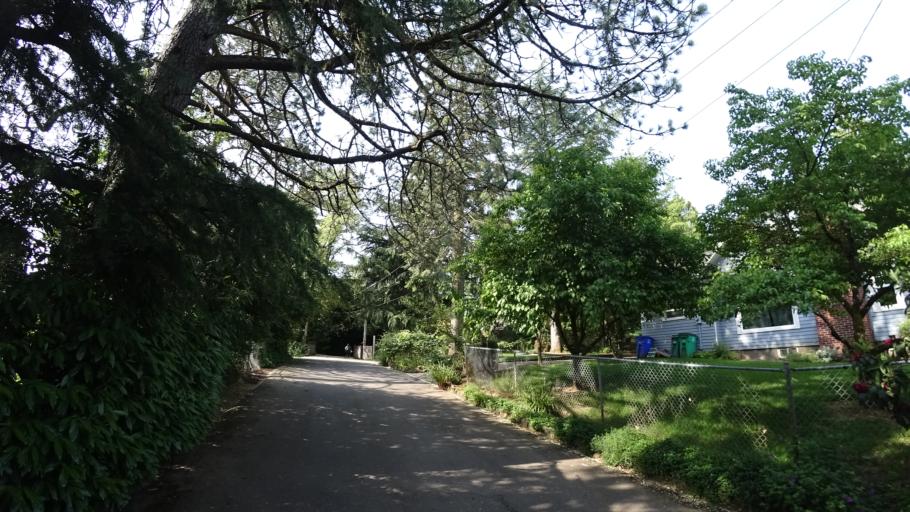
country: US
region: Oregon
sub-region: Washington County
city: Garden Home-Whitford
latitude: 45.4585
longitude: -122.7155
